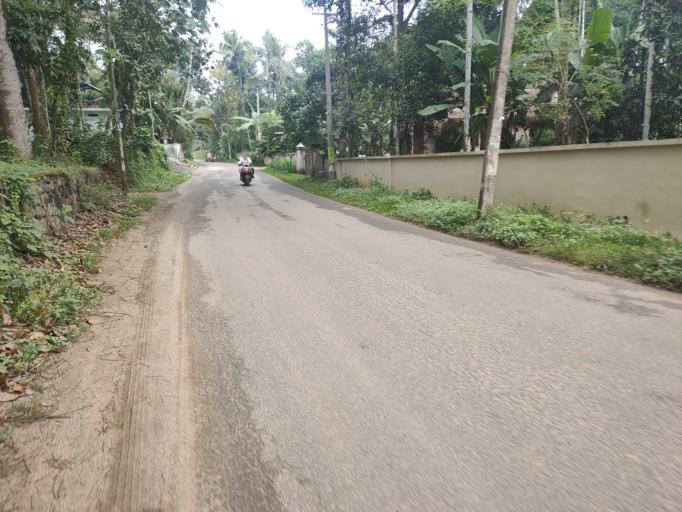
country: IN
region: Kerala
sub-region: Ernakulam
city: Muvattupula
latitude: 9.9930
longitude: 76.6369
